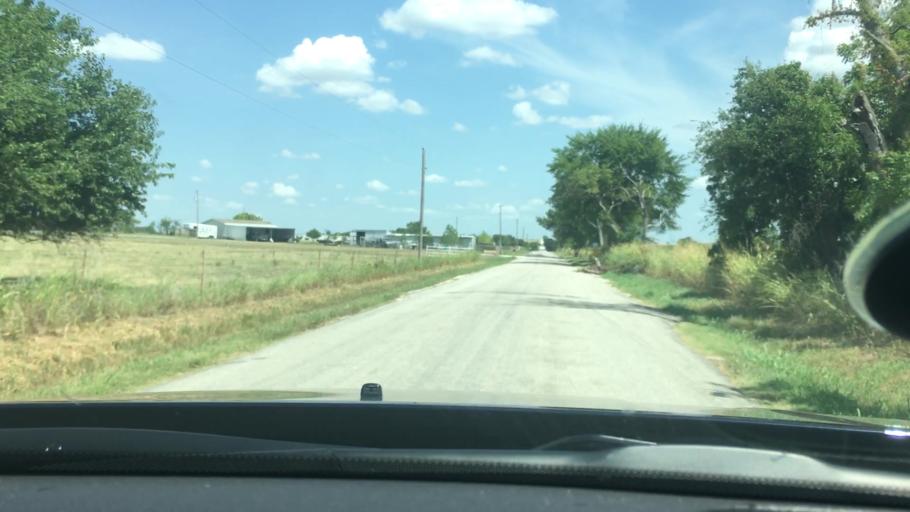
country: US
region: Oklahoma
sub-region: Love County
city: Marietta
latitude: 33.9410
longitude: -97.1869
